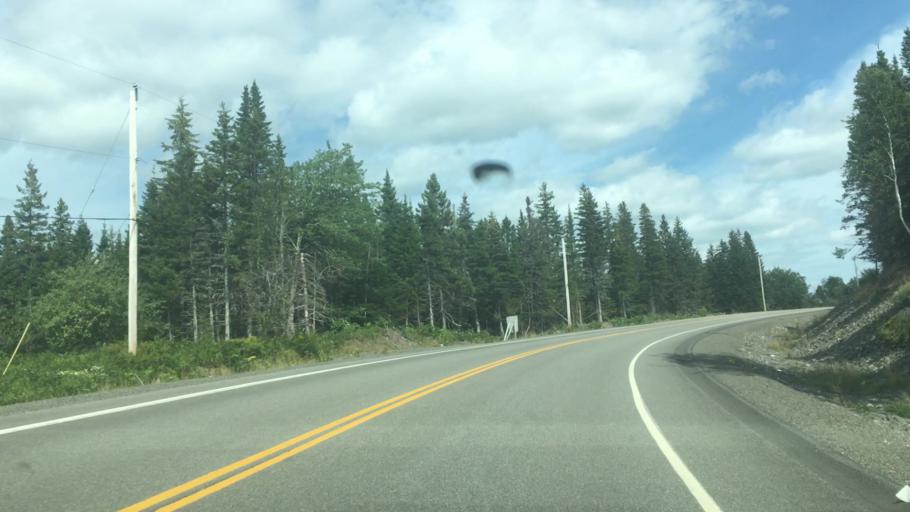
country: CA
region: Nova Scotia
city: Sydney Mines
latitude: 46.3265
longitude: -60.6061
